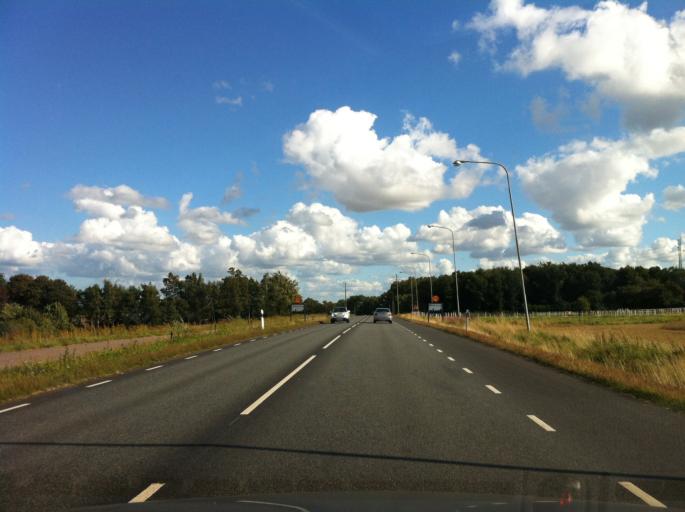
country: SE
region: Skane
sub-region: Bastads Kommun
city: Forslov
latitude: 56.3650
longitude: 12.8072
